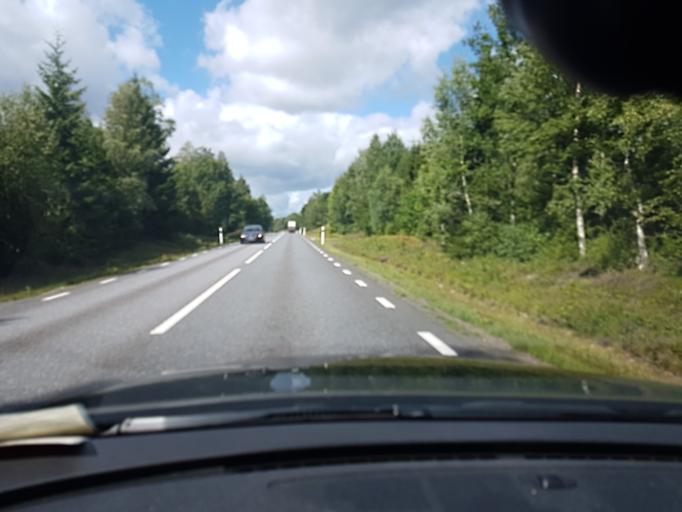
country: SE
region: Kalmar
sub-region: Emmaboda Kommun
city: Emmaboda
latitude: 56.7330
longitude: 15.4494
